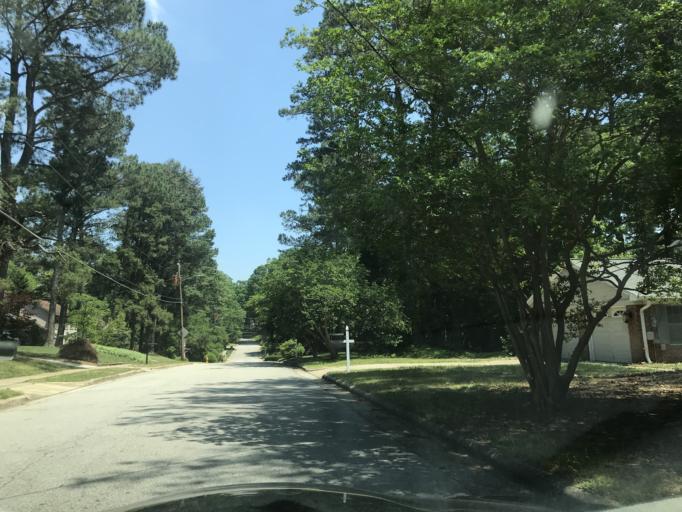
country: US
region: North Carolina
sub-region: Wake County
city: West Raleigh
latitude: 35.8467
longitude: -78.6187
